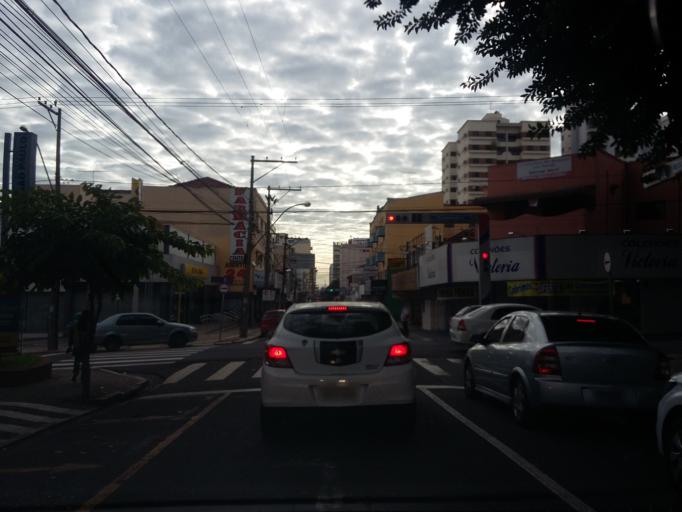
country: BR
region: Sao Paulo
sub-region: Sao Jose Do Rio Preto
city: Sao Jose do Rio Preto
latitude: -20.8154
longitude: -49.3850
